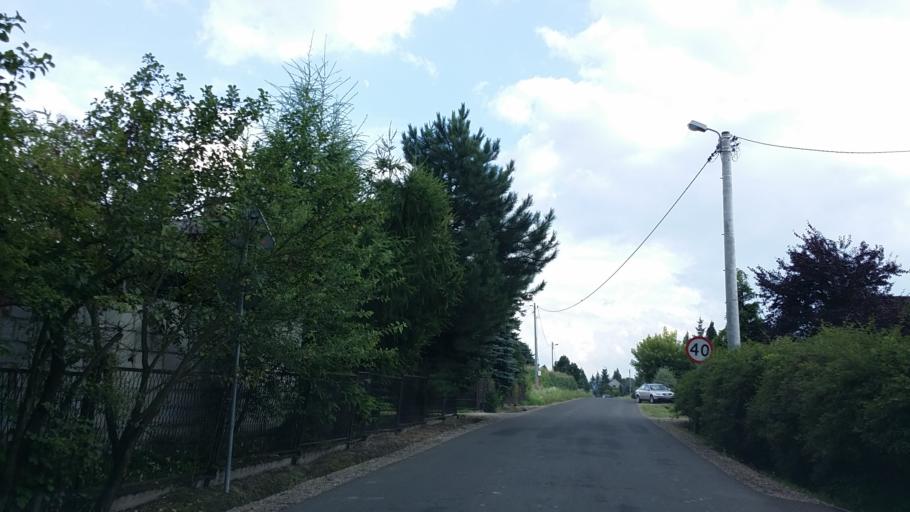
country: PL
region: Lesser Poland Voivodeship
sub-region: Powiat wadowicki
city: Bachowice
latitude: 49.9748
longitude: 19.4786
